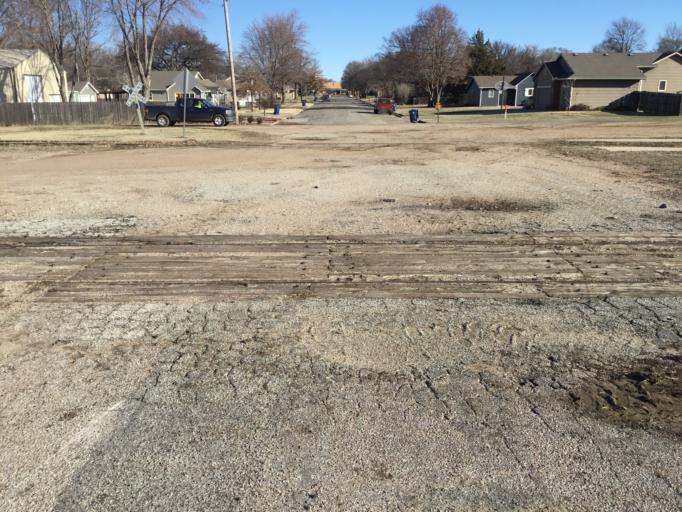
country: US
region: Kansas
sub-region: Sedgwick County
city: Saint Marys
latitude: 37.6562
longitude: -97.6813
